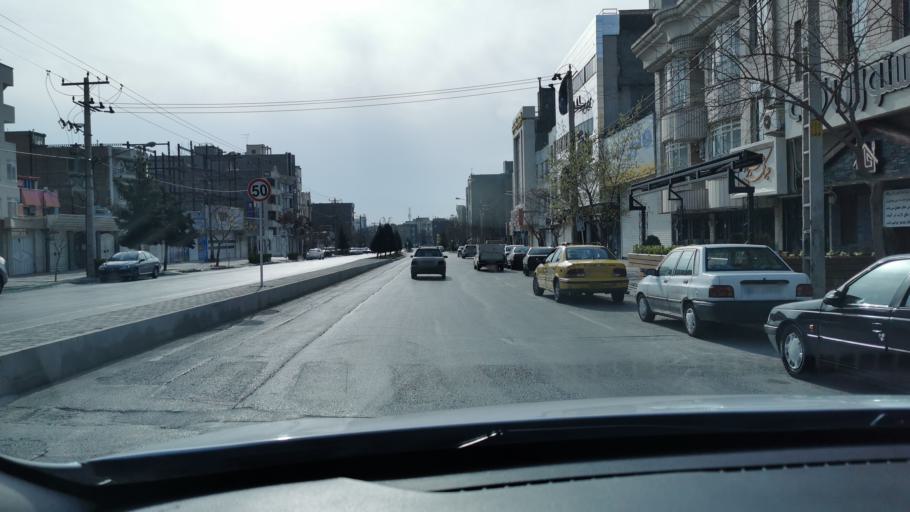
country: IR
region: Razavi Khorasan
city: Mashhad
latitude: 36.3157
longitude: 59.5092
